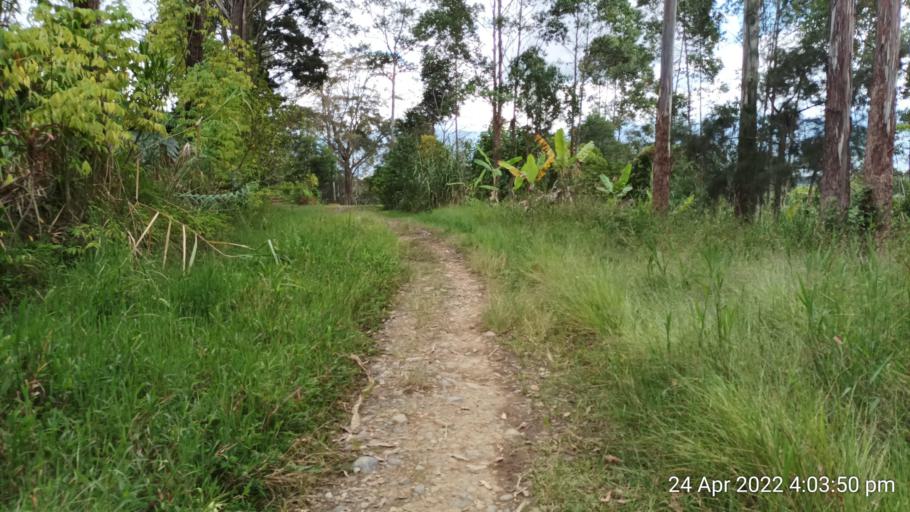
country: PG
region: Jiwaka
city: Minj
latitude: -5.9021
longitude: 144.8227
